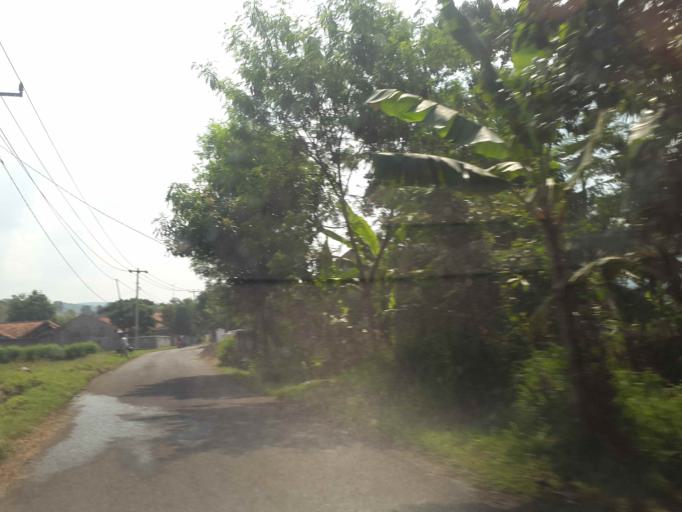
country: ID
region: West Java
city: Ciranjang-hilir
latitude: -6.7202
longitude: 107.1992
